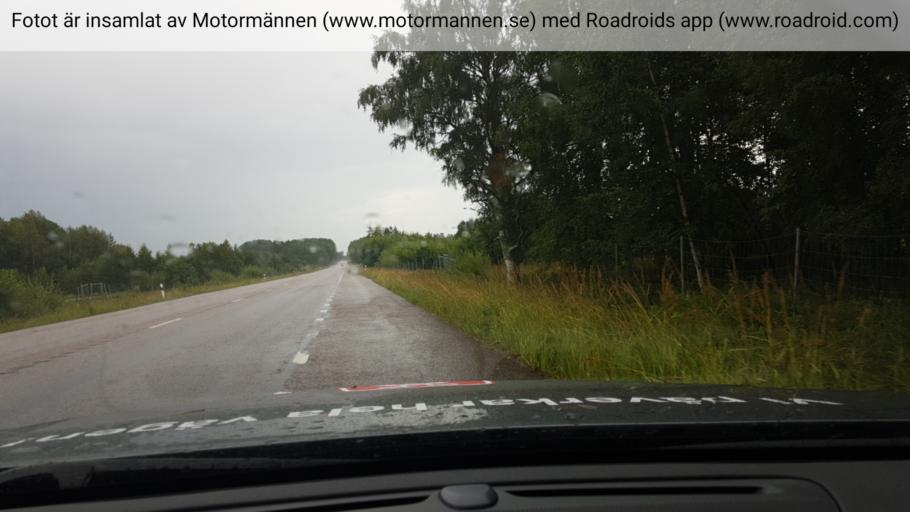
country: SE
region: Uppsala
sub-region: Alvkarleby Kommun
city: AElvkarleby
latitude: 60.5820
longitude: 17.4654
